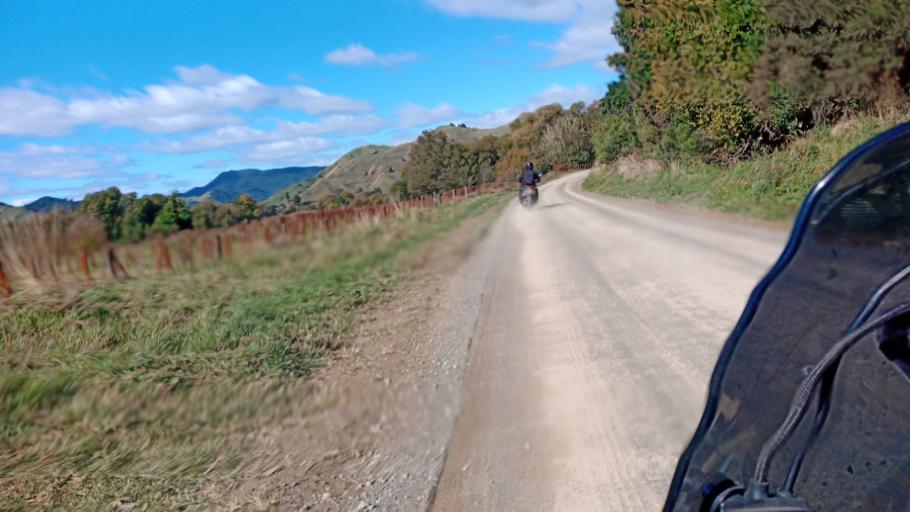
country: NZ
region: Bay of Plenty
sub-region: Opotiki District
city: Opotiki
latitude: -38.2560
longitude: 177.5531
